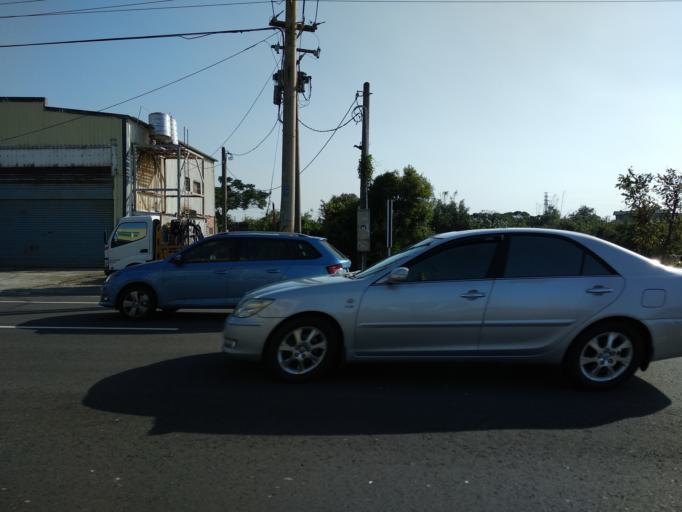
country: TW
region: Taiwan
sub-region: Hsinchu
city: Zhubei
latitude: 24.9879
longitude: 121.0402
